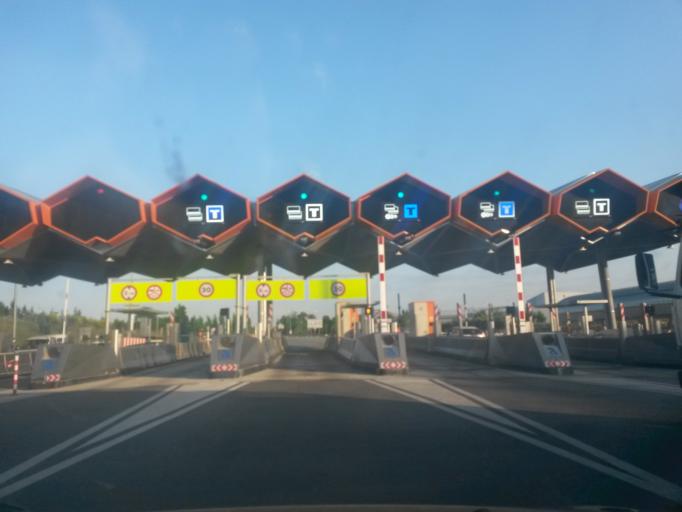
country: ES
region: Catalonia
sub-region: Provincia de Girona
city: Salt
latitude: 41.9918
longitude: 2.7937
